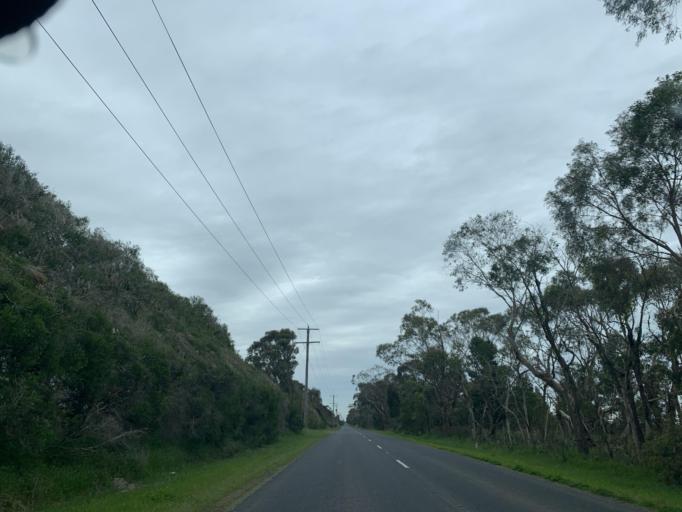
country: AU
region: Victoria
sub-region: Cardinia
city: Garfield
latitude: -38.0838
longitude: 145.6042
